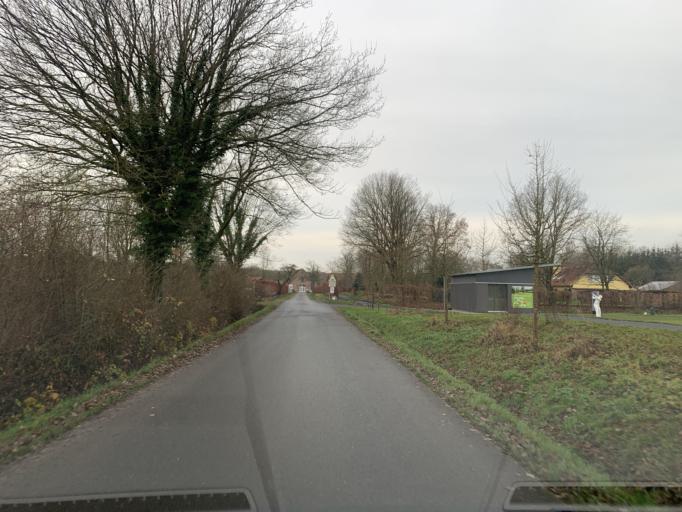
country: DE
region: North Rhine-Westphalia
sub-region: Regierungsbezirk Munster
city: Senden
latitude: 51.8970
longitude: 7.5496
